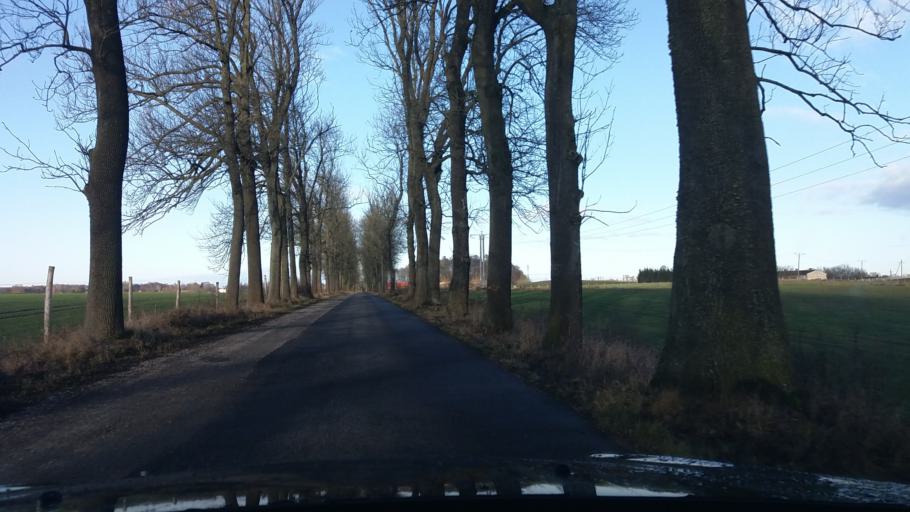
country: PL
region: West Pomeranian Voivodeship
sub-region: Powiat choszczenski
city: Drawno
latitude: 53.2055
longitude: 15.7769
